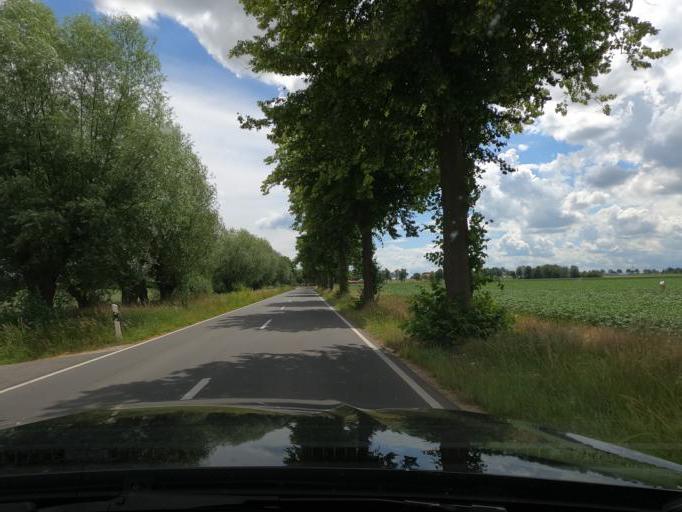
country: DE
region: Lower Saxony
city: Hohenhameln
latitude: 52.2547
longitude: 10.0185
